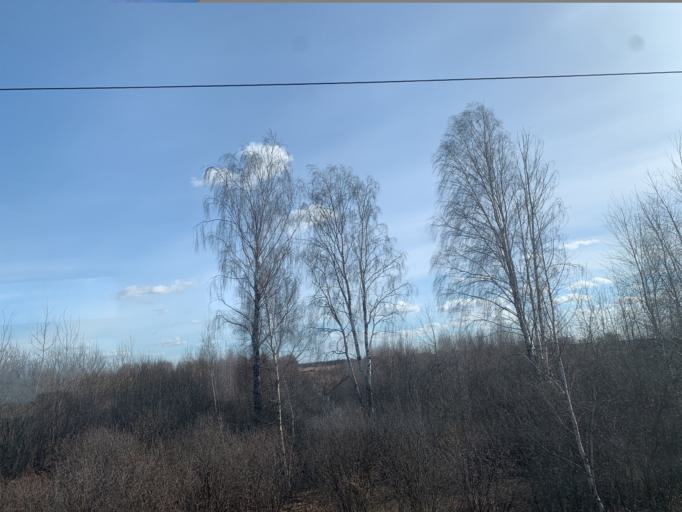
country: BY
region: Minsk
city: Stan'kava
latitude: 53.6870
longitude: 27.2224
